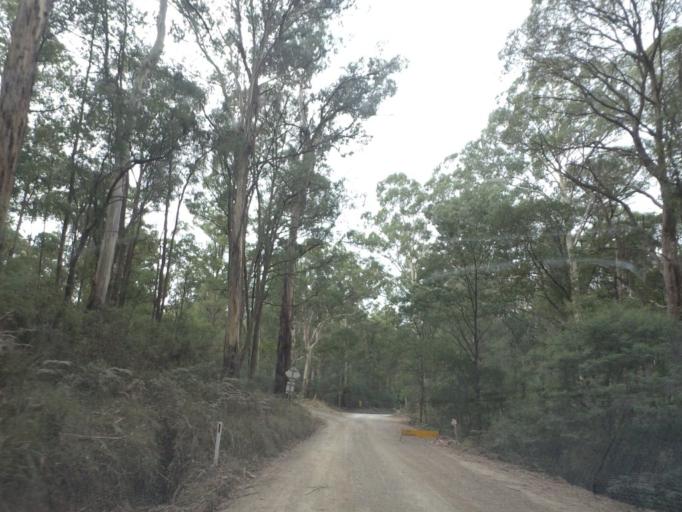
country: AU
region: Victoria
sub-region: Murrindindi
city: Alexandra
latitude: -37.4834
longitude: 145.9684
